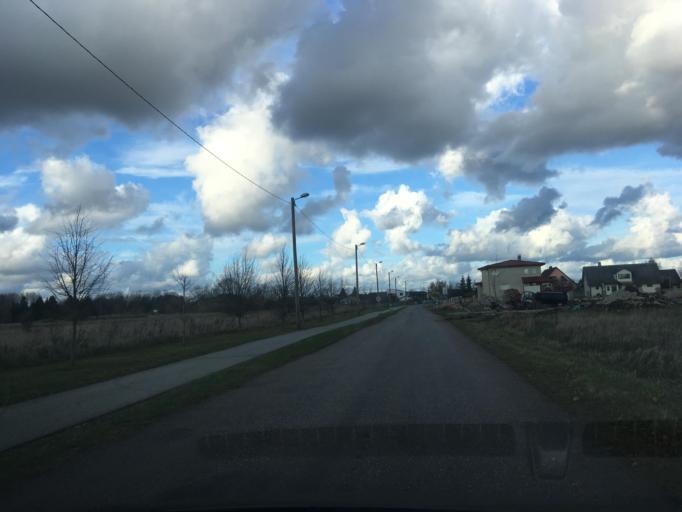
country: EE
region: Harju
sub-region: Joelaehtme vald
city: Loo
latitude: 59.4387
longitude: 24.9601
